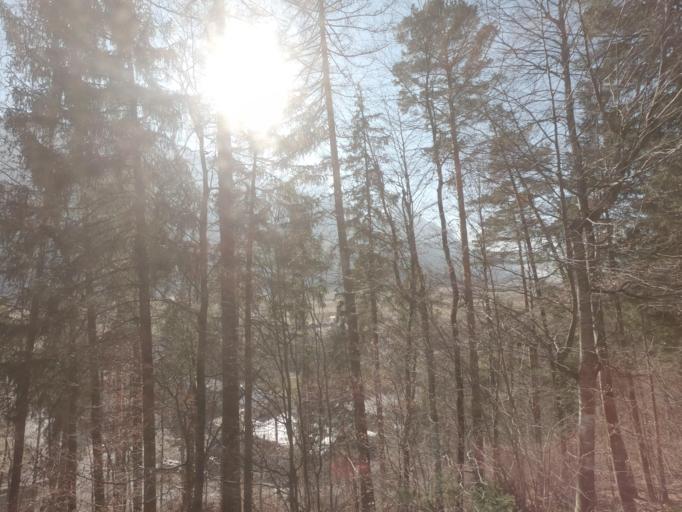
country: CH
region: Bern
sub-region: Interlaken-Oberhasli District
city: Meiringen
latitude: 46.7400
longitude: 8.1687
